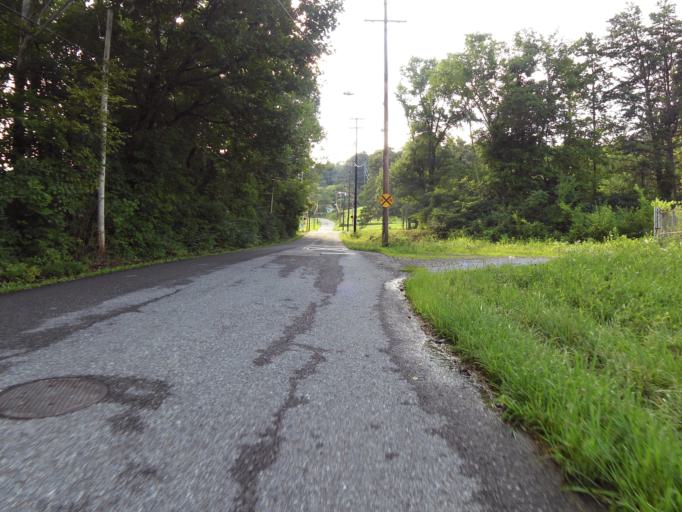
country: US
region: Tennessee
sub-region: Knox County
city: Knoxville
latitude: 36.0081
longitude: -83.9276
